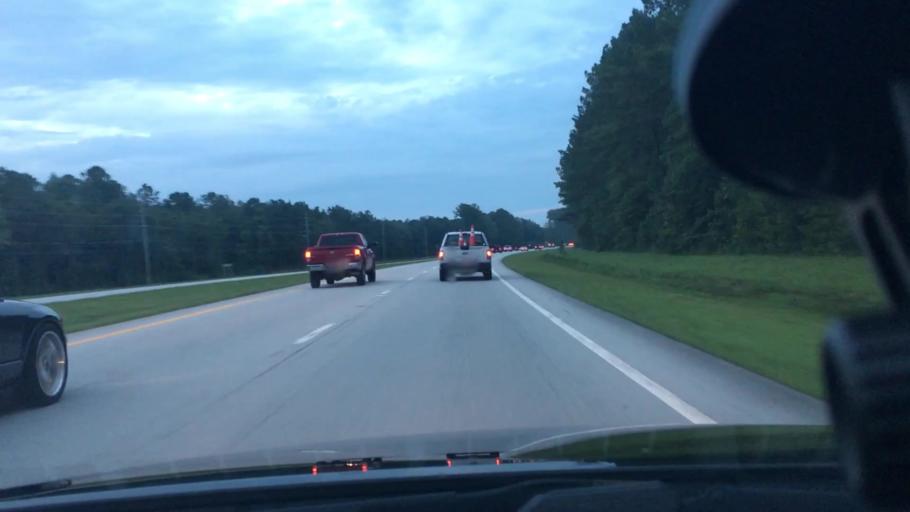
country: US
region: North Carolina
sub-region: Craven County
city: Neuse Forest
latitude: 34.9623
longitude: -76.9557
